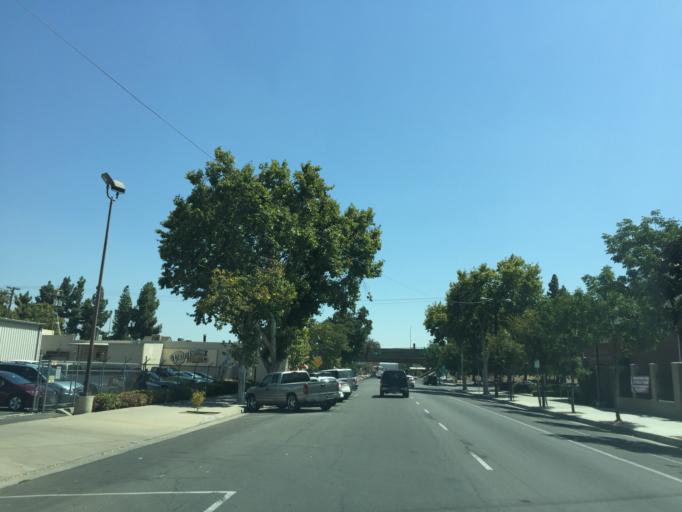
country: US
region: California
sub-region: Fresno County
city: Fresno
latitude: 36.7318
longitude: -119.7823
